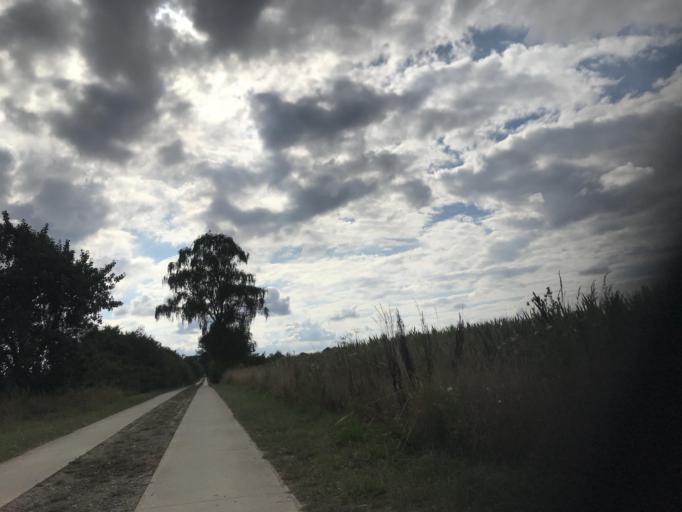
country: DE
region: Lower Saxony
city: Reinstorf
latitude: 53.2537
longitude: 10.5777
